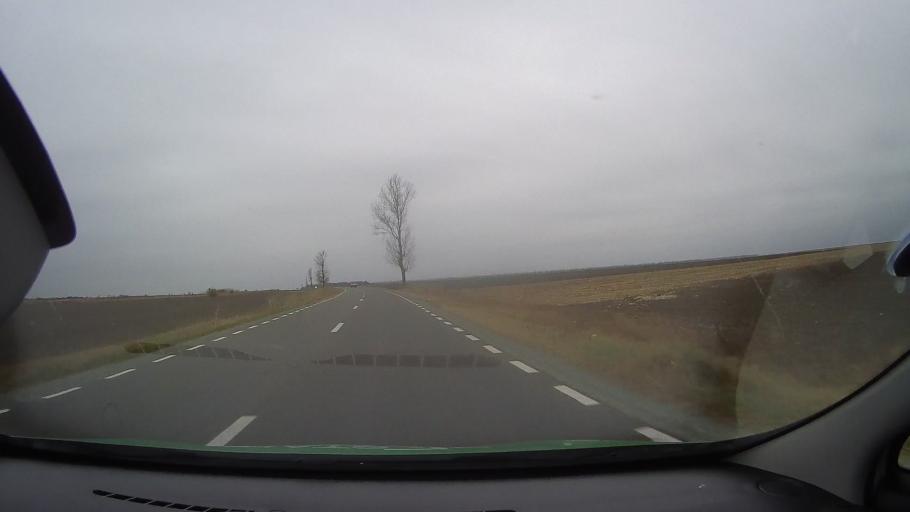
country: RO
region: Ialomita
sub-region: Comuna Scanteia
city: Iazu
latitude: 44.7156
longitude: 27.4196
